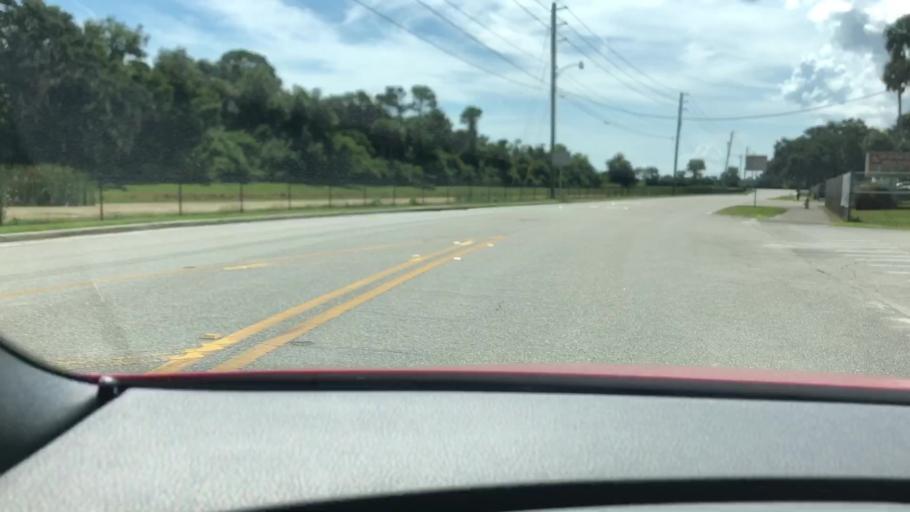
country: US
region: Florida
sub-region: Volusia County
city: New Smyrna Beach
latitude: 29.0056
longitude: -80.9230
